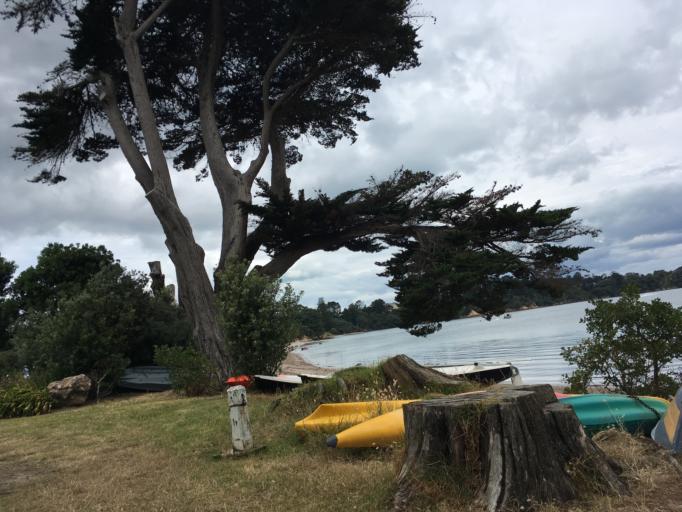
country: NZ
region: Auckland
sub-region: Auckland
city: Pakuranga
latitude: -36.7931
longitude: 175.0219
